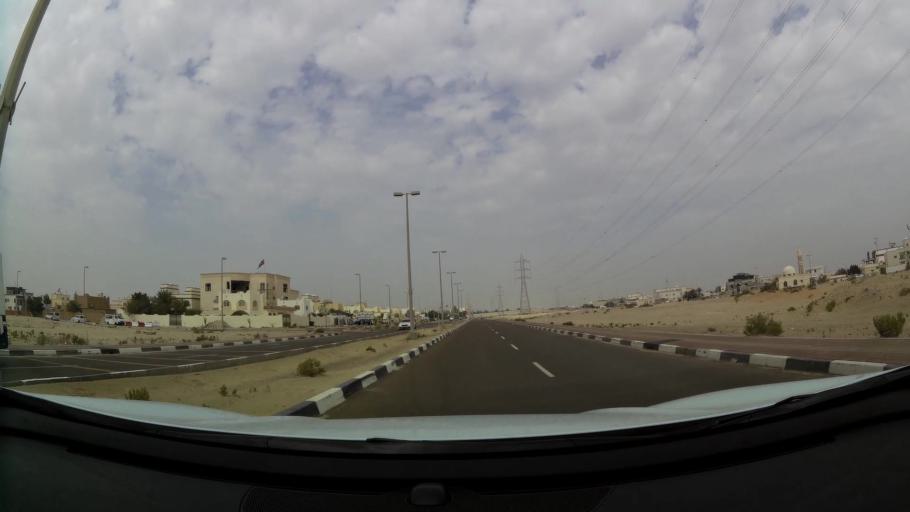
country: AE
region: Abu Dhabi
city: Abu Dhabi
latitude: 24.3208
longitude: 54.6296
